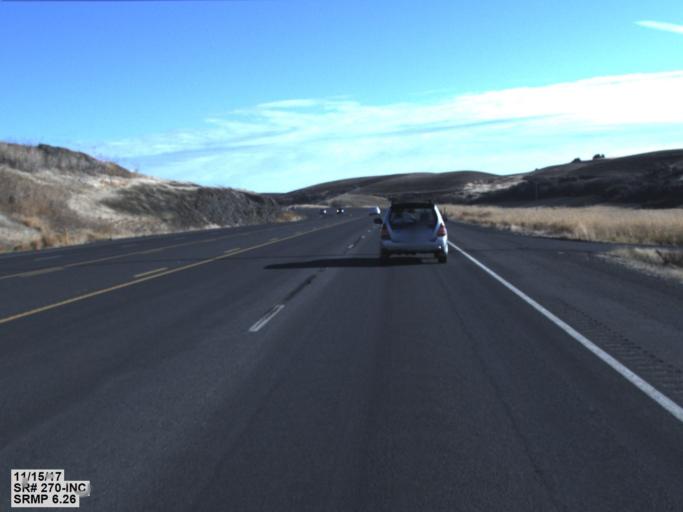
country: US
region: Washington
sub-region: Whitman County
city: Pullman
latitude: 46.7279
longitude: -117.1104
